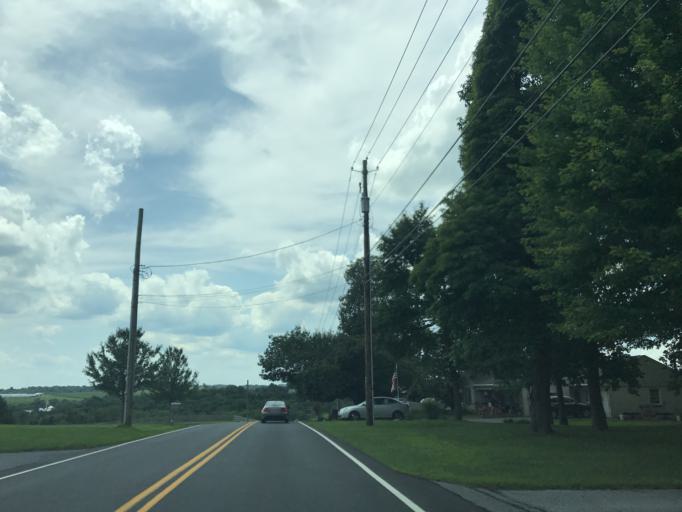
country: US
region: Pennsylvania
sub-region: Lancaster County
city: Penryn
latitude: 40.2066
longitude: -76.3871
